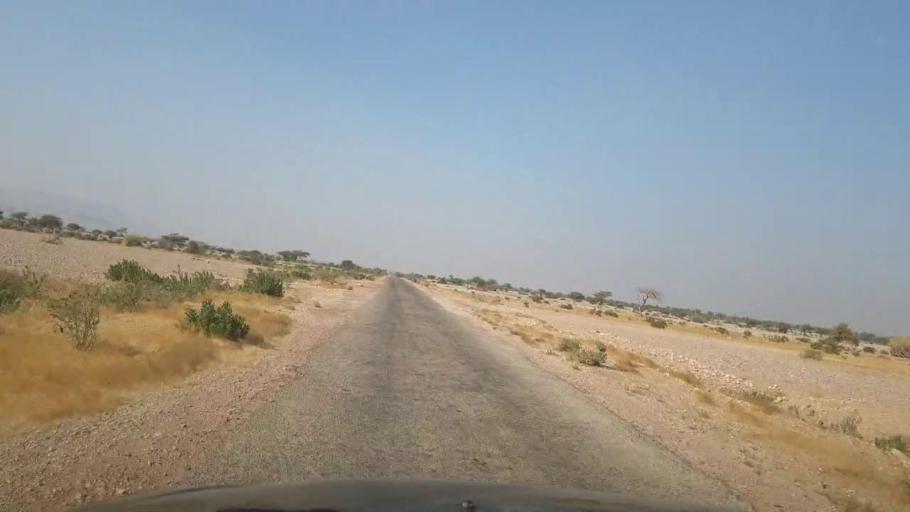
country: PK
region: Sindh
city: Jamshoro
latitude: 25.5796
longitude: 67.8217
